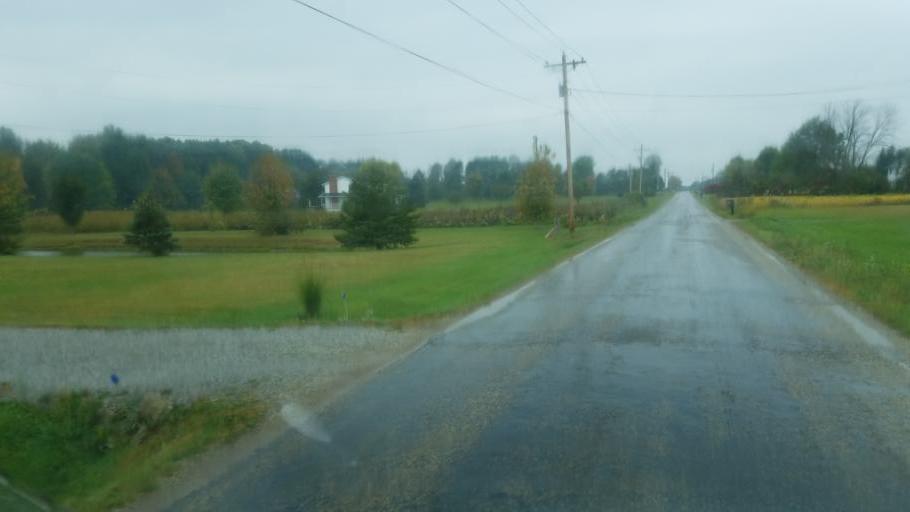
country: US
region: Ohio
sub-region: Ashland County
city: Ashland
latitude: 40.8145
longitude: -82.3443
